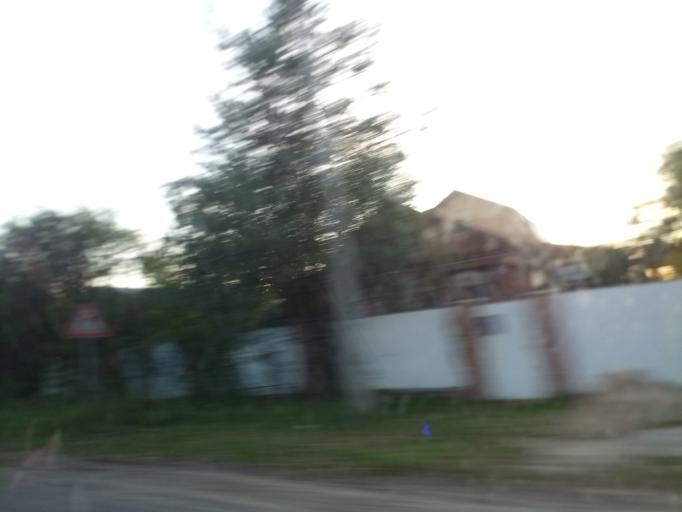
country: RU
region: Moskovskaya
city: Noginsk-9
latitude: 56.0666
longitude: 38.5586
